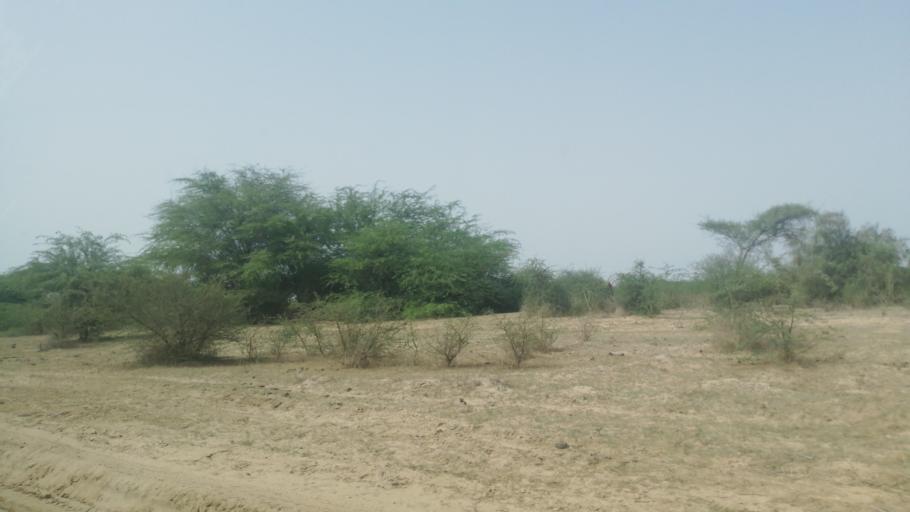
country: SN
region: Saint-Louis
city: Saint-Louis
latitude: 16.0643
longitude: -16.3166
